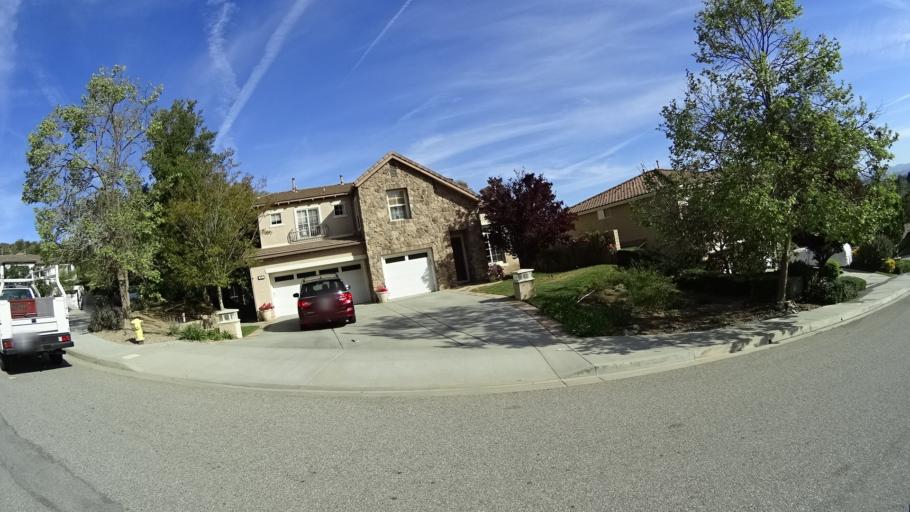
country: US
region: California
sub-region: Ventura County
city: Casa Conejo
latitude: 34.1664
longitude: -118.9646
